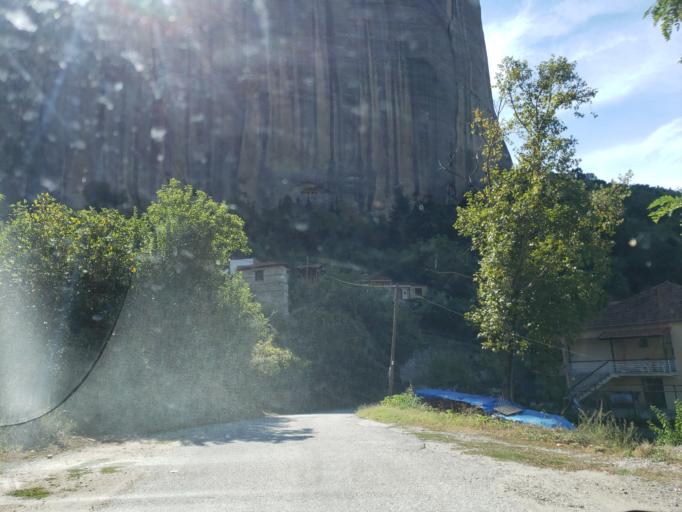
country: GR
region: Thessaly
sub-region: Trikala
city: Kastraki
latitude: 39.7154
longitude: 21.6227
